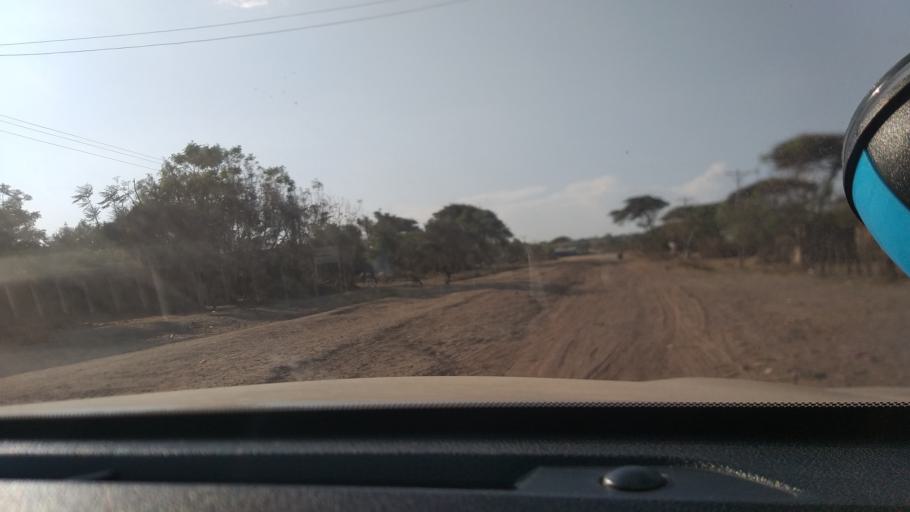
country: ET
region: Oromiya
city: Shashemene
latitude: 7.4907
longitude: 38.7179
